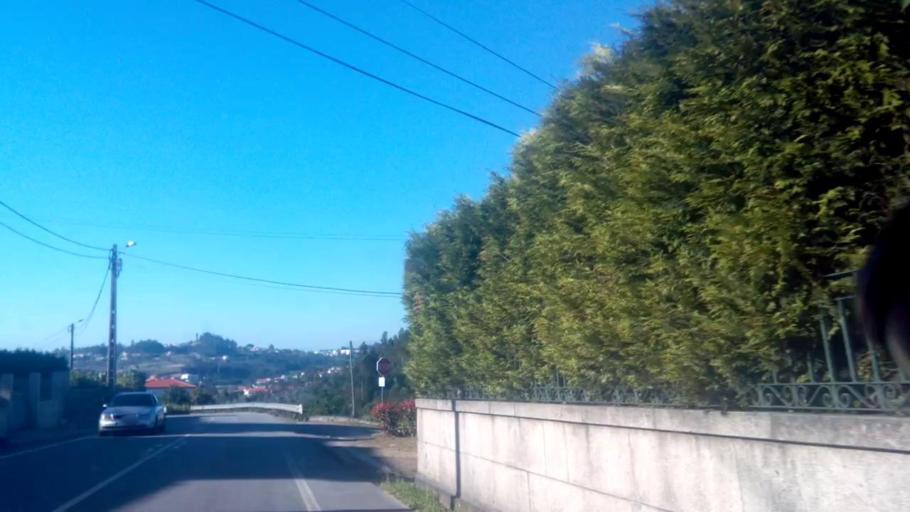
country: PT
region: Porto
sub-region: Penafiel
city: Penafiel
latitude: 41.1914
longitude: -8.2737
